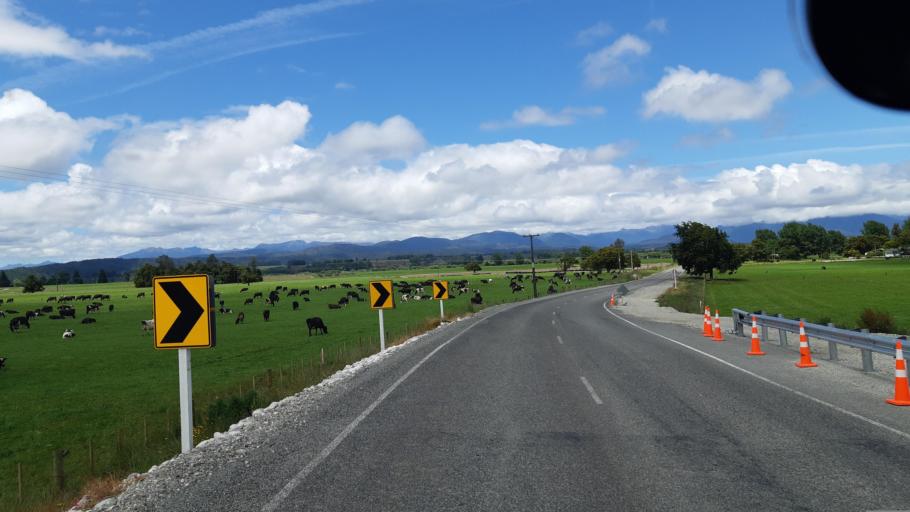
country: NZ
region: West Coast
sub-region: Grey District
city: Greymouth
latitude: -42.2650
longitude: 171.6570
